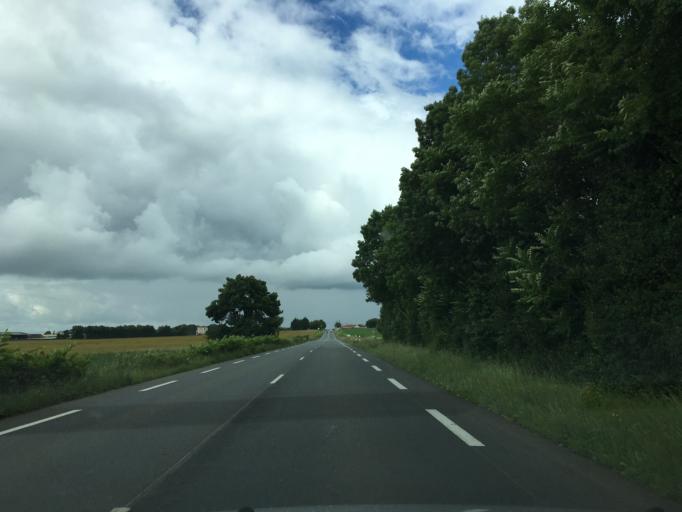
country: FR
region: Poitou-Charentes
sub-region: Departement de la Charente-Maritime
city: Saint-Jean-d'Angely
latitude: 46.0669
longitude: -0.5078
